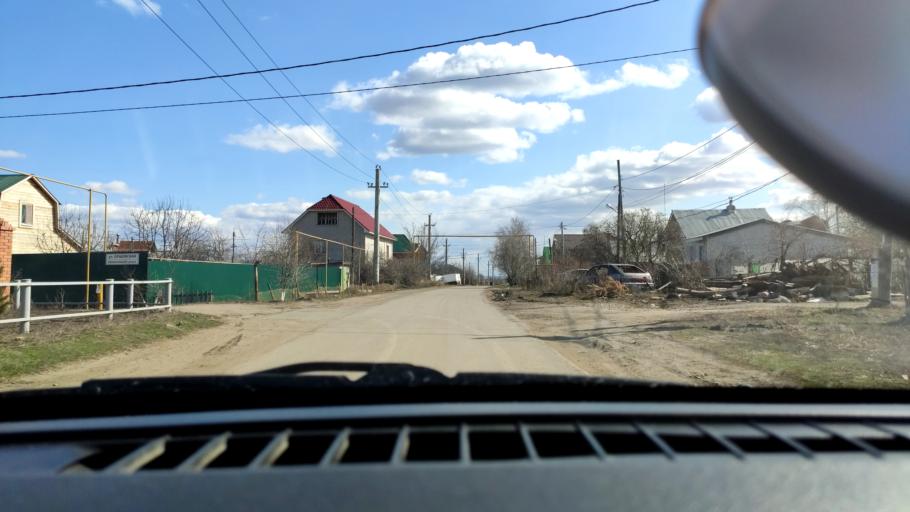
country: RU
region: Samara
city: Petra-Dubrava
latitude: 53.2931
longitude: 50.3103
